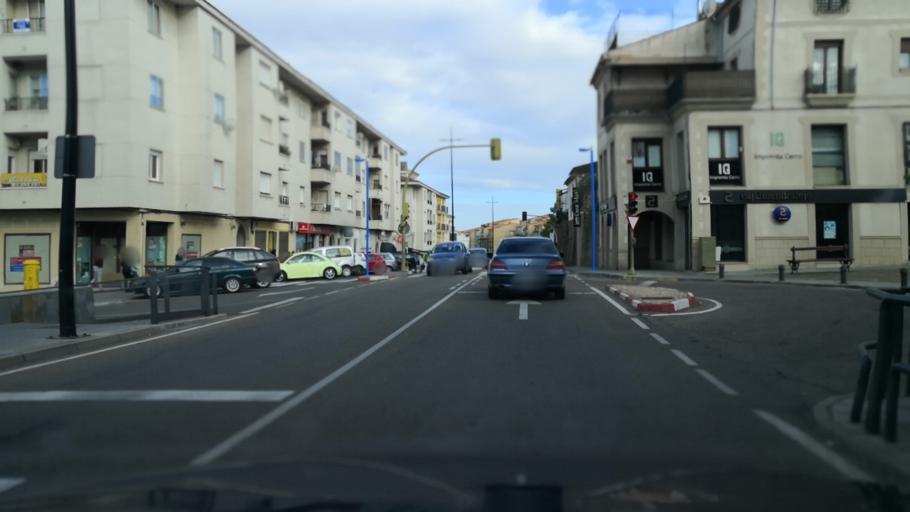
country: ES
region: Extremadura
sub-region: Provincia de Caceres
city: Coria
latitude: 39.9842
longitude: -6.5349
